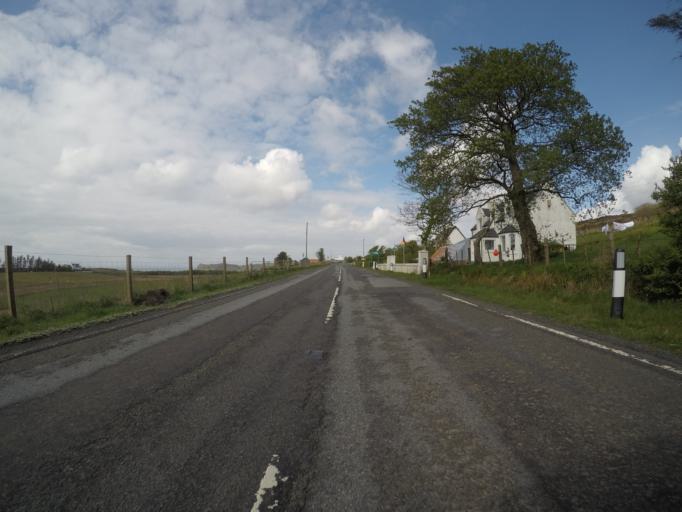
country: GB
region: Scotland
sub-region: Highland
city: Portree
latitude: 57.5645
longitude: -6.3645
